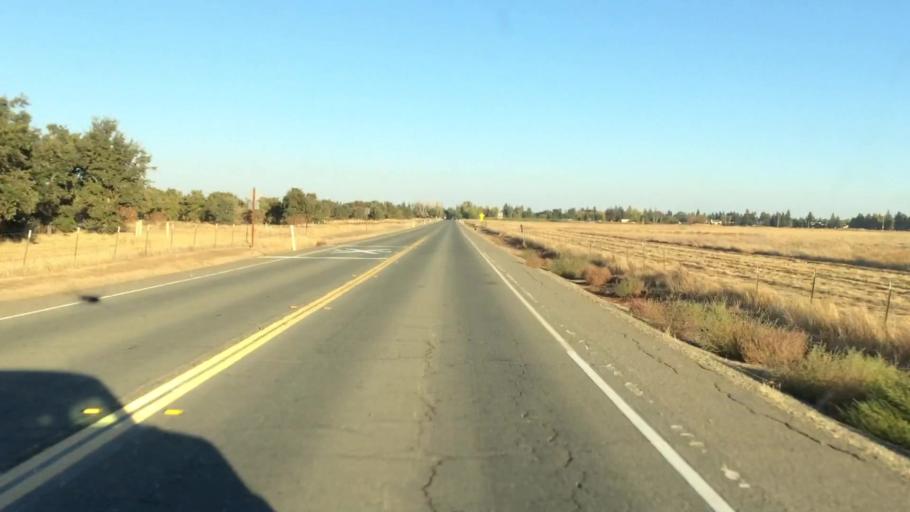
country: US
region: California
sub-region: Sacramento County
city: Laguna
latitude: 38.4377
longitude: -121.4570
